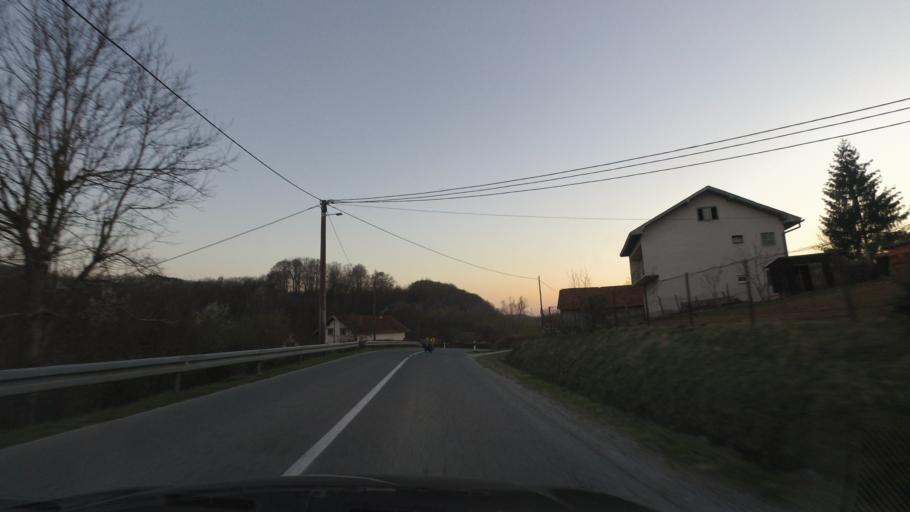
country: HR
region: Karlovacka
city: Vojnic
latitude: 45.3348
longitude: 15.7198
